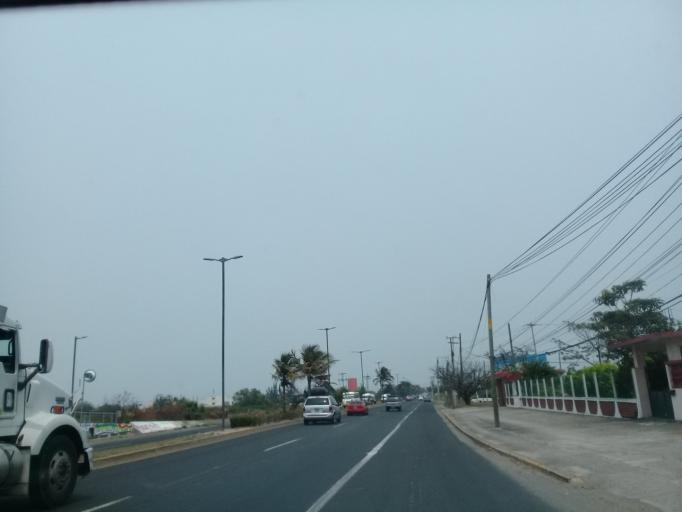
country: MX
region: Veracruz
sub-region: Veracruz
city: Hacienda Sotavento
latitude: 19.1495
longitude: -96.1733
